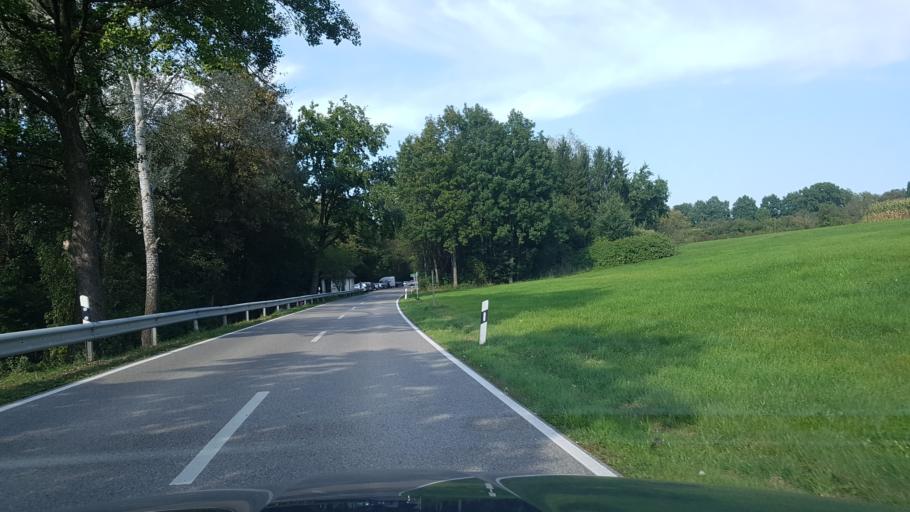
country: DE
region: Bavaria
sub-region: Upper Bavaria
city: Laufen
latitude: 47.9059
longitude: 12.9128
